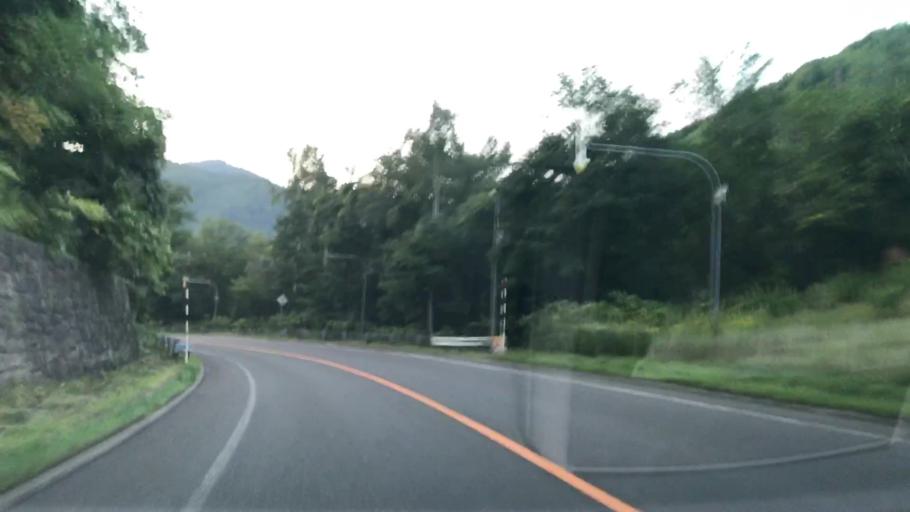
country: JP
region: Hokkaido
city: Sapporo
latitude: 42.9204
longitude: 141.1252
